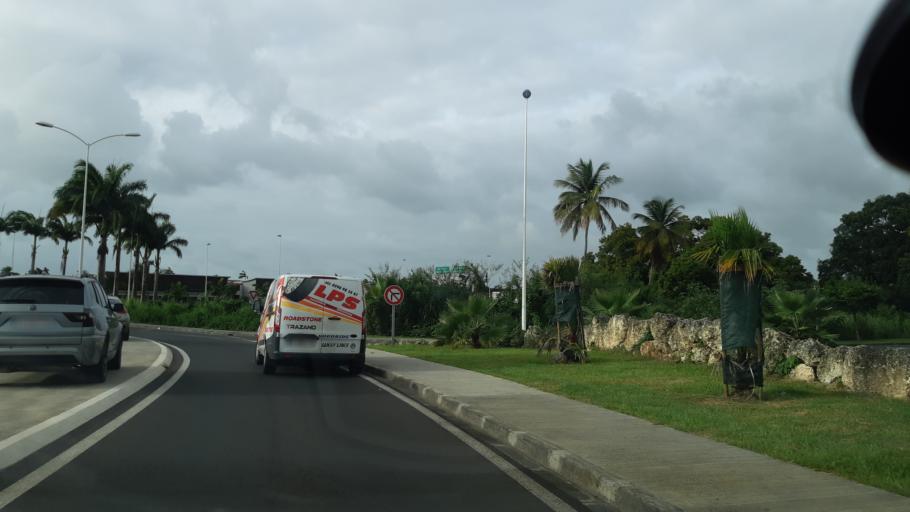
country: GP
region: Guadeloupe
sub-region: Guadeloupe
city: Les Abymes
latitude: 16.2726
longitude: -61.5240
